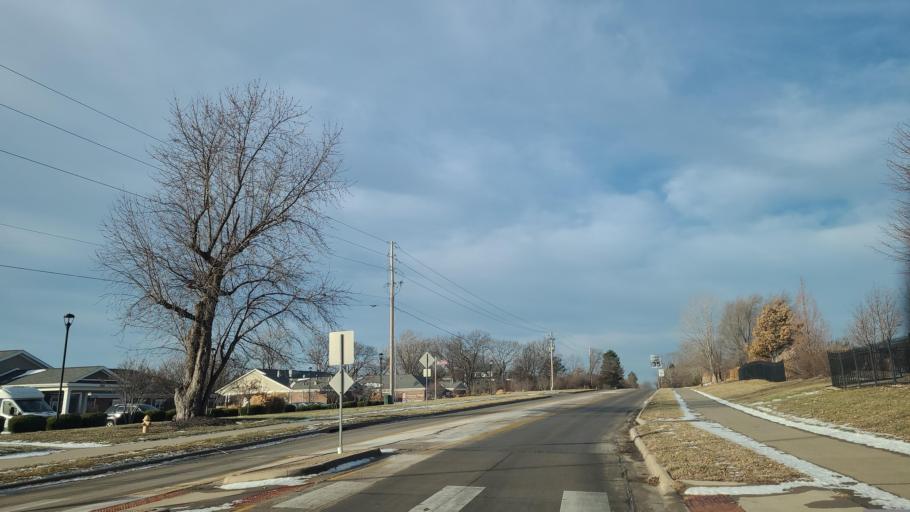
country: US
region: Kansas
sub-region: Douglas County
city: Lawrence
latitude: 38.9862
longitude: -95.2886
